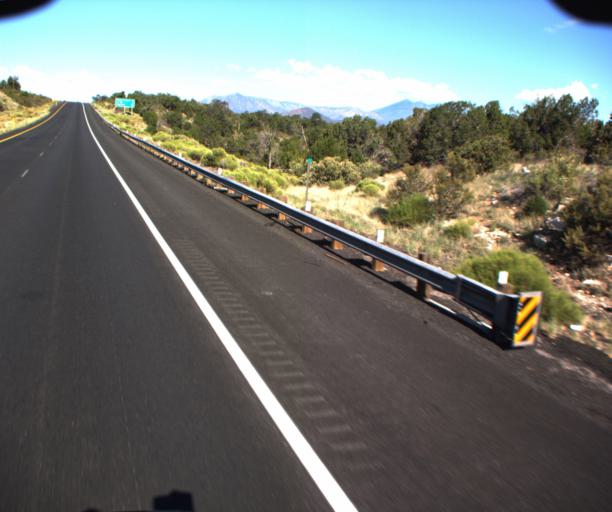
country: US
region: Arizona
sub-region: Coconino County
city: Flagstaff
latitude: 35.2018
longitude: -111.4291
